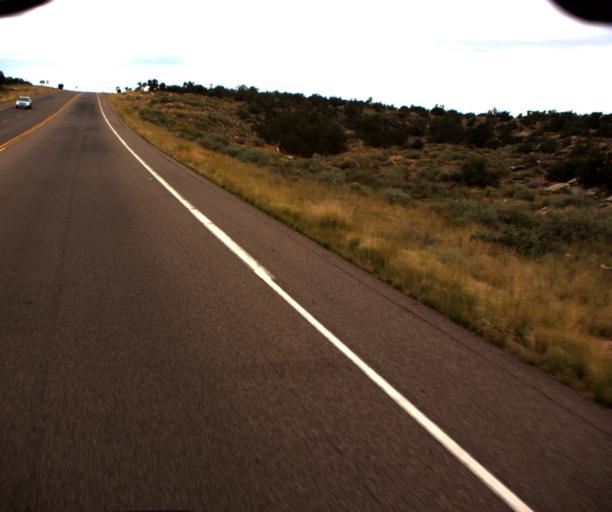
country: US
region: Arizona
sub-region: Navajo County
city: Snowflake
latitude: 34.5736
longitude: -110.0831
